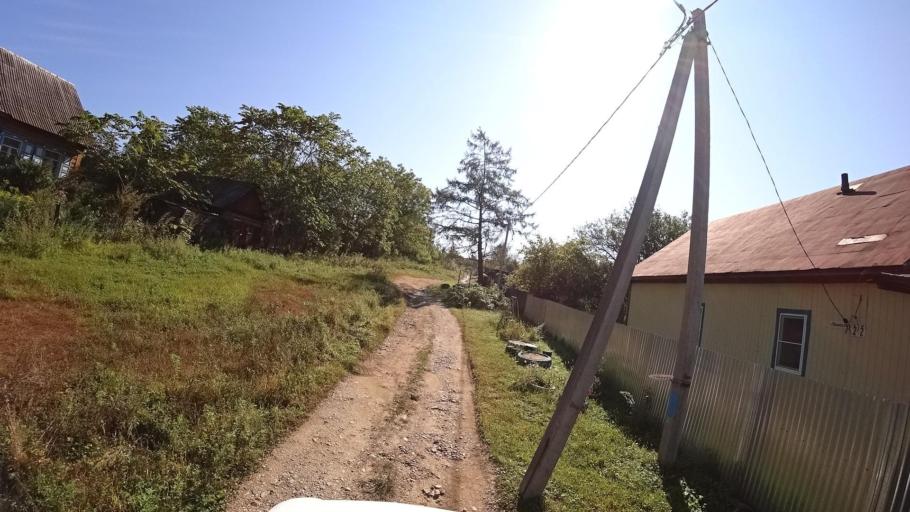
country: RU
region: Jewish Autonomous Oblast
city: Bira
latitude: 49.0060
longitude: 132.4648
